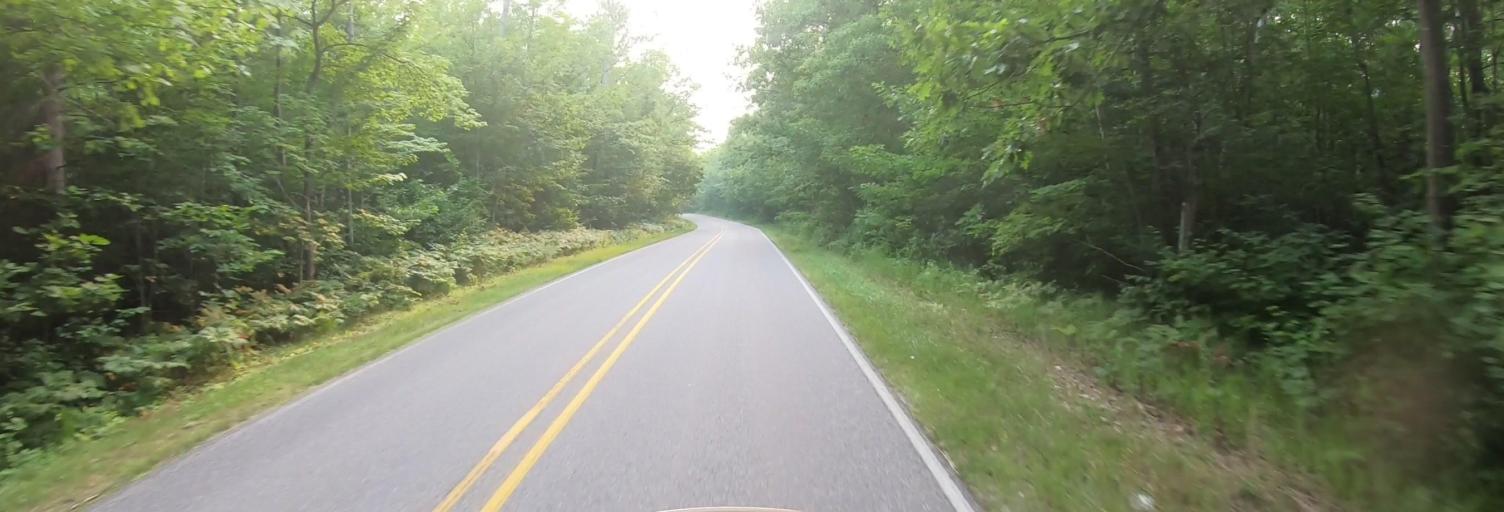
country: US
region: Michigan
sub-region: Chippewa County
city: Sault Ste. Marie
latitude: 46.4577
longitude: -84.7501
